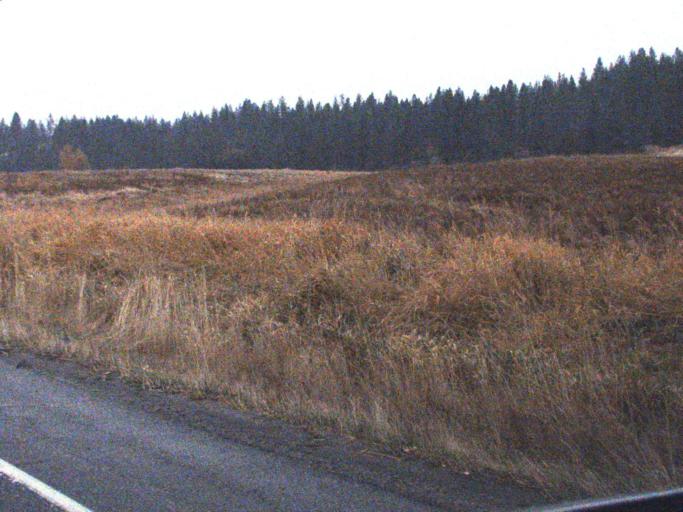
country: US
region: Washington
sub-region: Stevens County
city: Kettle Falls
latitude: 48.5893
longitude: -117.9902
